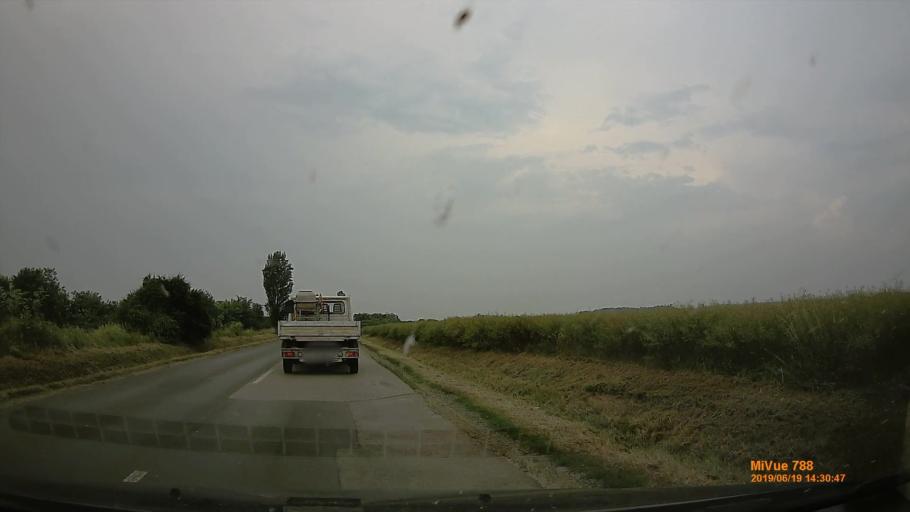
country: HU
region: Baranya
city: Szigetvar
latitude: 46.0659
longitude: 17.7707
